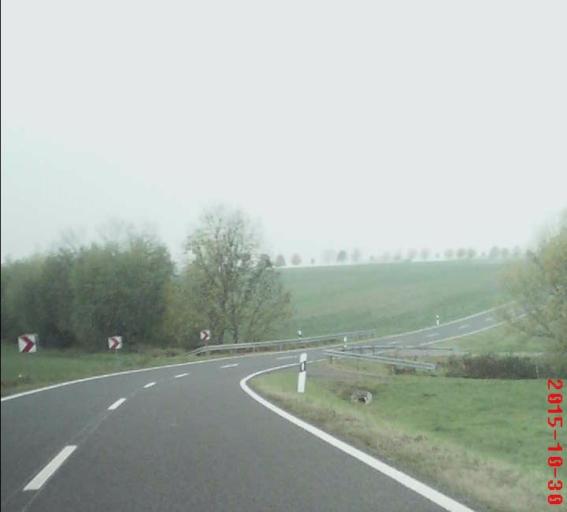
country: DE
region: Thuringia
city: Anrode
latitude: 51.2431
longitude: 10.3653
